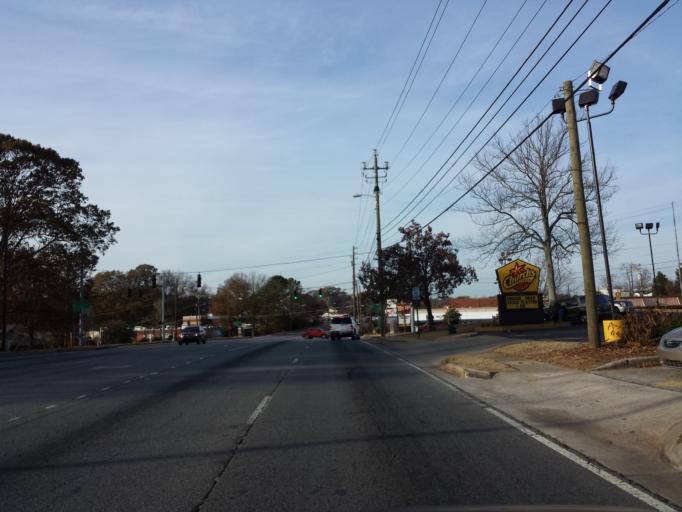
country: US
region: Georgia
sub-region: Cobb County
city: Marietta
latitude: 33.9493
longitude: -84.5509
